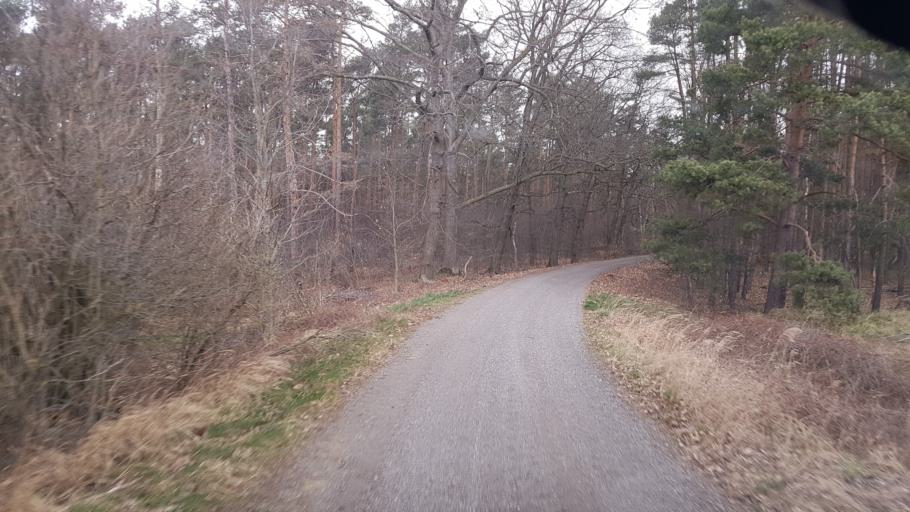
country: DE
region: Brandenburg
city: Finsterwalde
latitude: 51.5777
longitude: 13.7001
